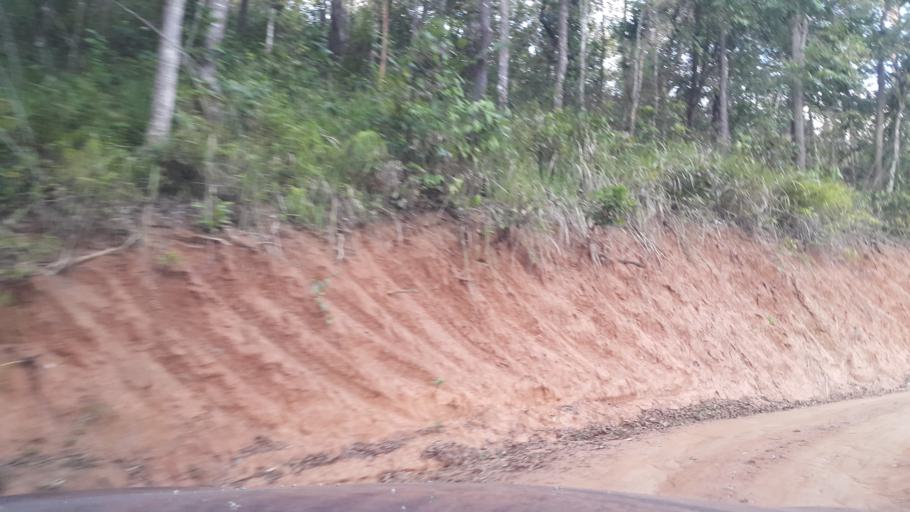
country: TH
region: Chiang Mai
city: Samoeng
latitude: 19.0069
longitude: 98.6596
